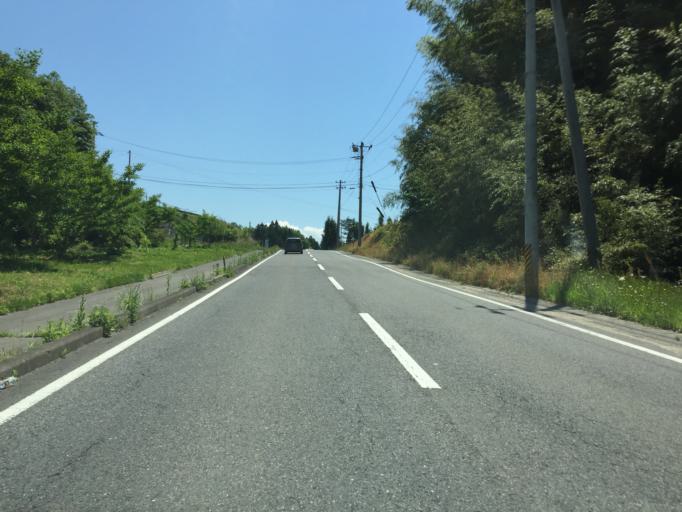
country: JP
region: Fukushima
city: Motomiya
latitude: 37.5218
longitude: 140.4562
